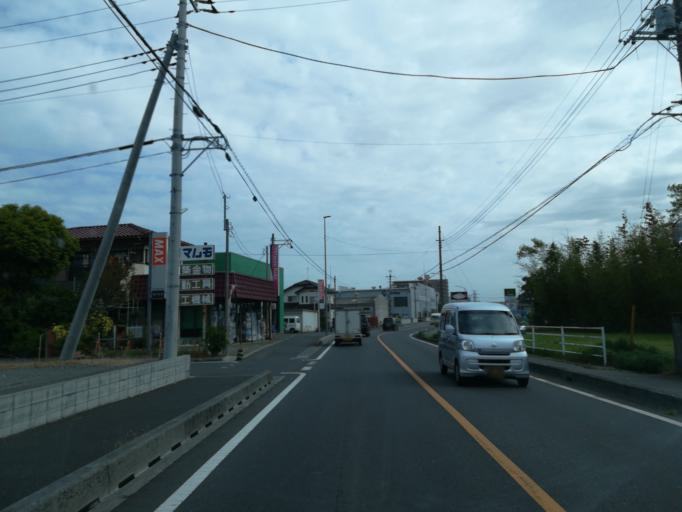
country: JP
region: Saitama
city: Satte
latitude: 36.0609
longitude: 139.7045
